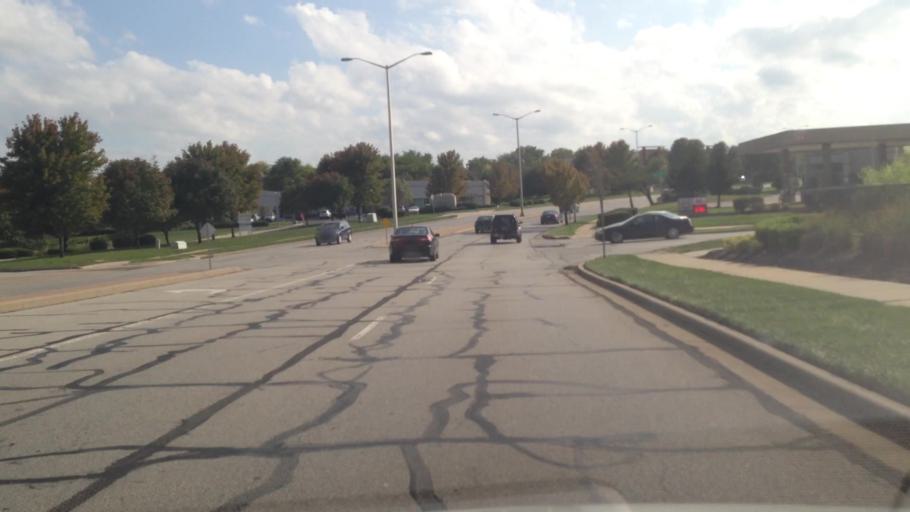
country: US
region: Kansas
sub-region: Johnson County
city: Lenexa
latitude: 38.9260
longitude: -94.7545
